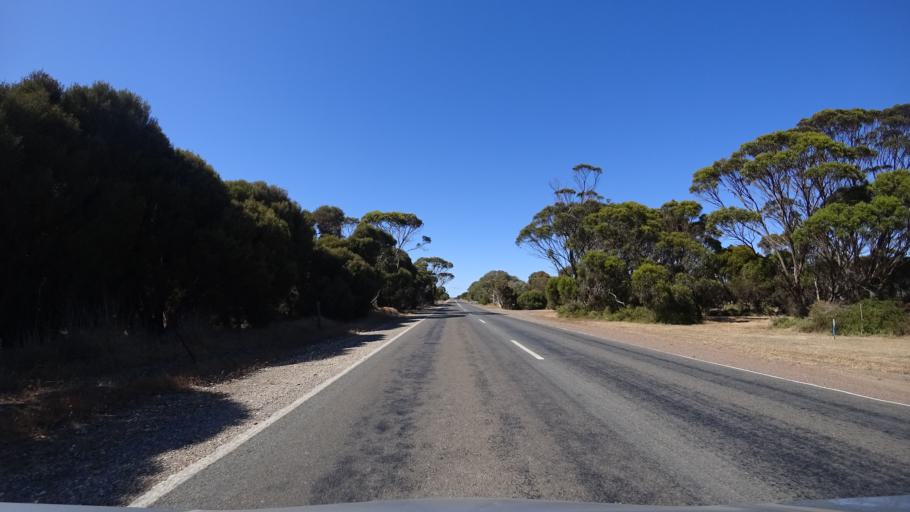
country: AU
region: South Australia
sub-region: Kangaroo Island
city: Kingscote
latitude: -35.6825
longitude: 137.5729
